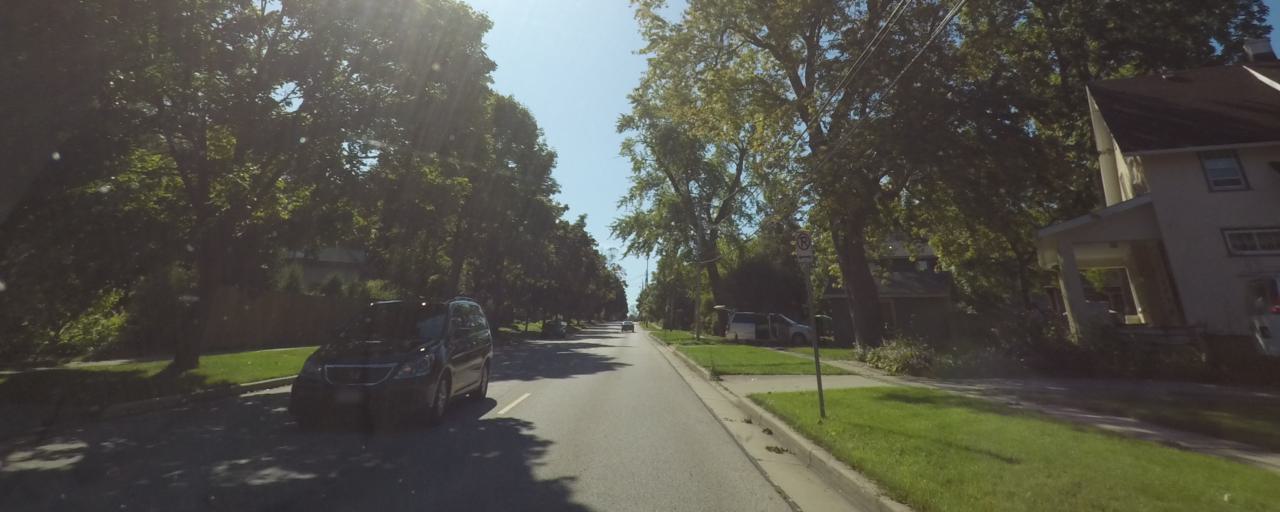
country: US
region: Wisconsin
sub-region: Waukesha County
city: Waukesha
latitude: 43.0065
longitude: -88.2194
